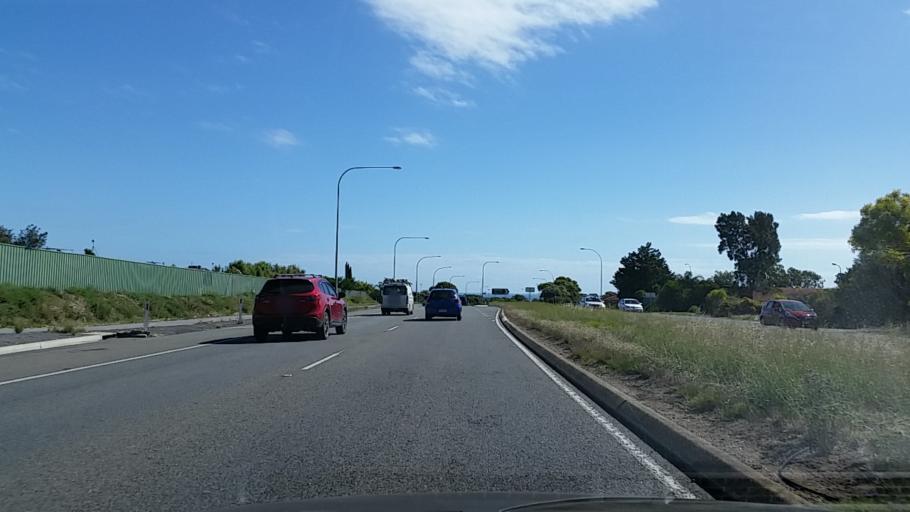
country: AU
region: South Australia
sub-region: Marion
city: Happy Valley
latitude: -35.0827
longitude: 138.5120
